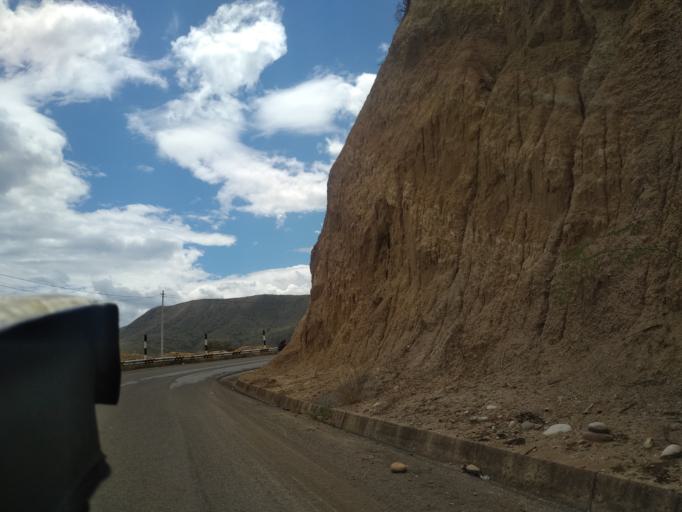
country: PE
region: Cajamarca
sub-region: Provincia de San Ignacio
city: La Coipa
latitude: -5.3709
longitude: -78.7783
